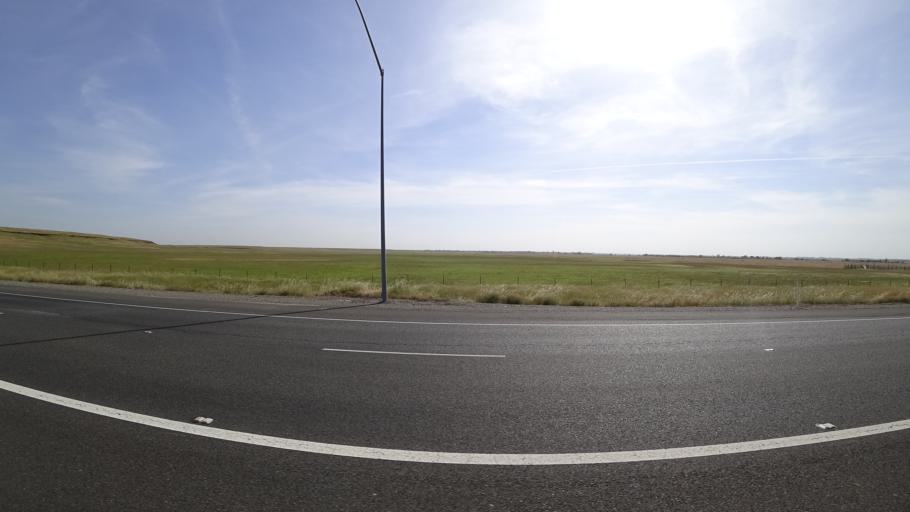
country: US
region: California
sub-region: Butte County
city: Durham
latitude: 39.6249
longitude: -121.6966
